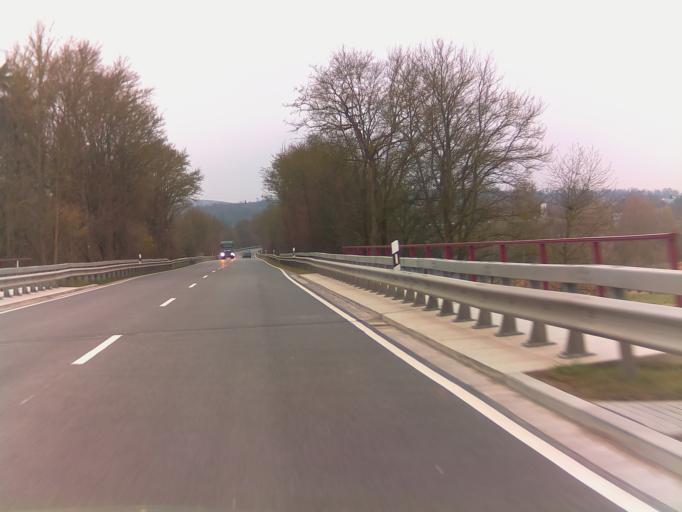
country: DE
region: Rheinland-Pfalz
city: Gau-Bickelheim
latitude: 49.8384
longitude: 8.0345
